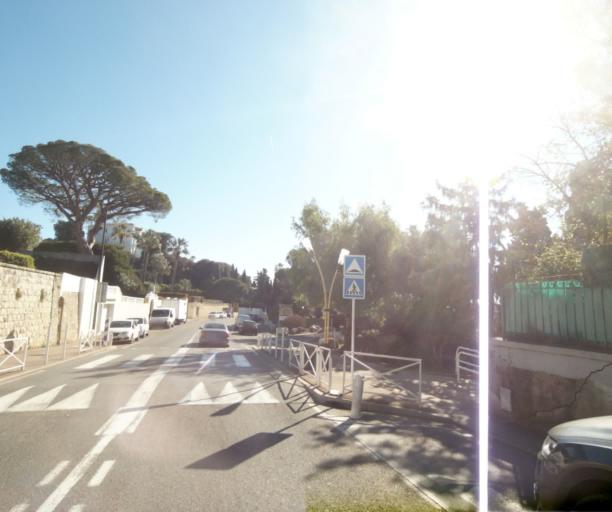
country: FR
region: Provence-Alpes-Cote d'Azur
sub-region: Departement des Alpes-Maritimes
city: Antibes
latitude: 43.5636
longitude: 7.1166
